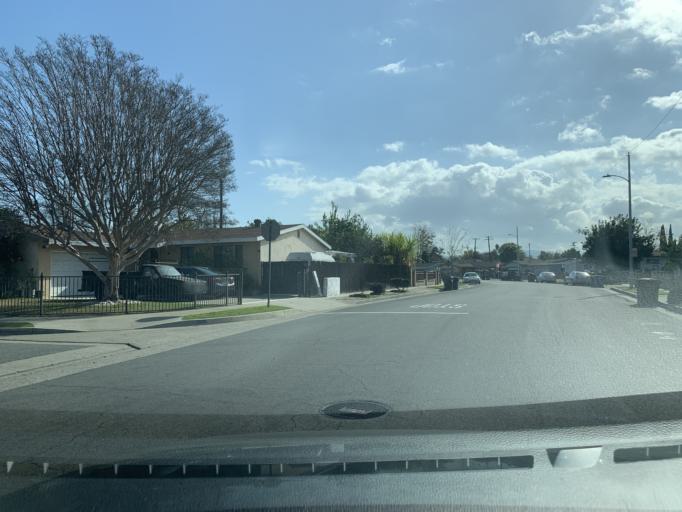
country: US
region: California
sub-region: Los Angeles County
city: South El Monte
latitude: 34.0674
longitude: -118.0542
